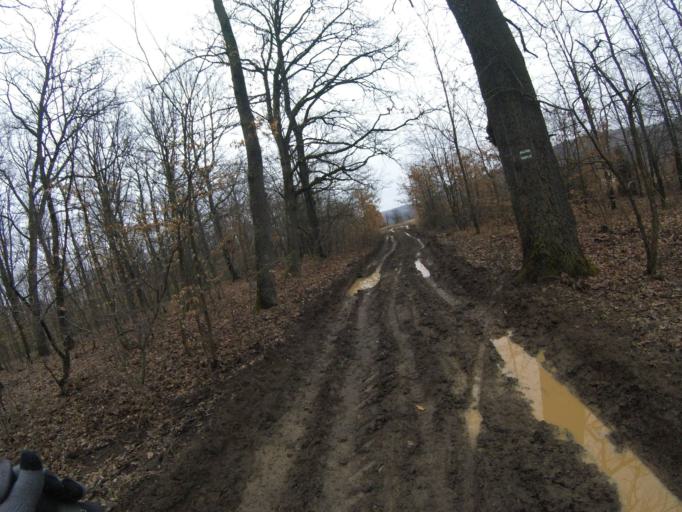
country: HU
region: Borsod-Abauj-Zemplen
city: Rudabanya
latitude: 48.4575
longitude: 20.5855
